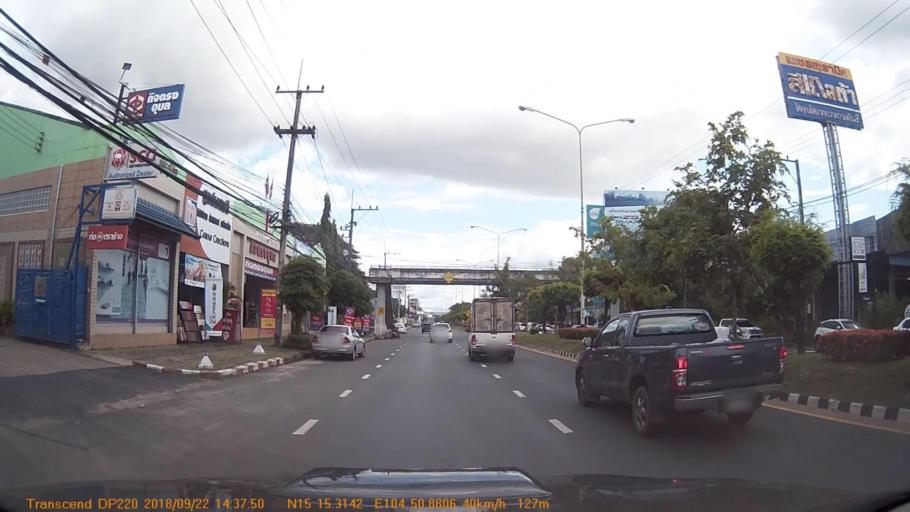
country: TH
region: Changwat Ubon Ratchathani
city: Ubon Ratchathani
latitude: 15.2550
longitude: 104.8481
